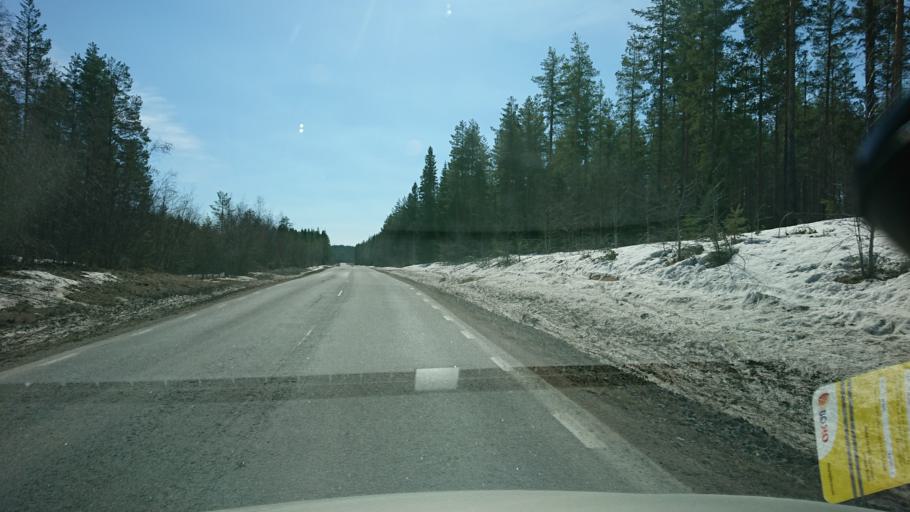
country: SE
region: Vaesternorrland
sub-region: Solleftea Kommun
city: As
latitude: 63.5934
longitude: 16.4300
